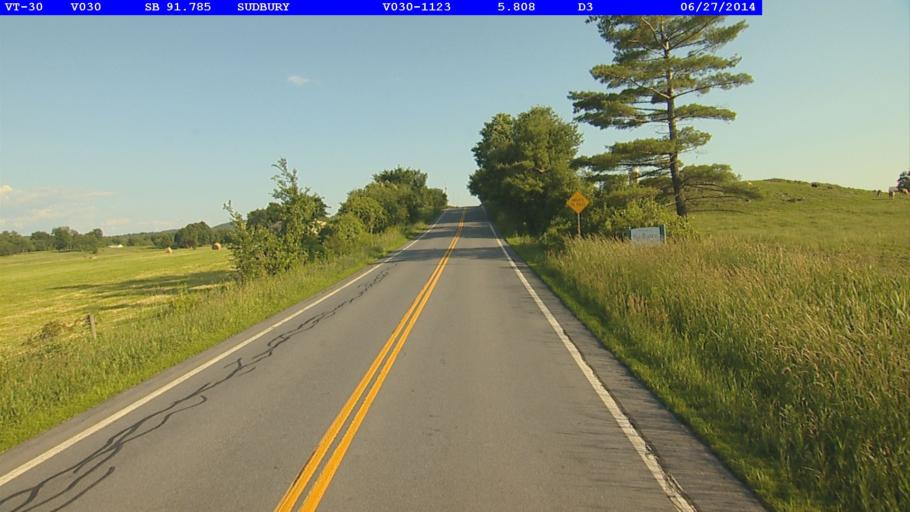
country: US
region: Vermont
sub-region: Rutland County
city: Brandon
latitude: 43.8298
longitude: -73.1935
